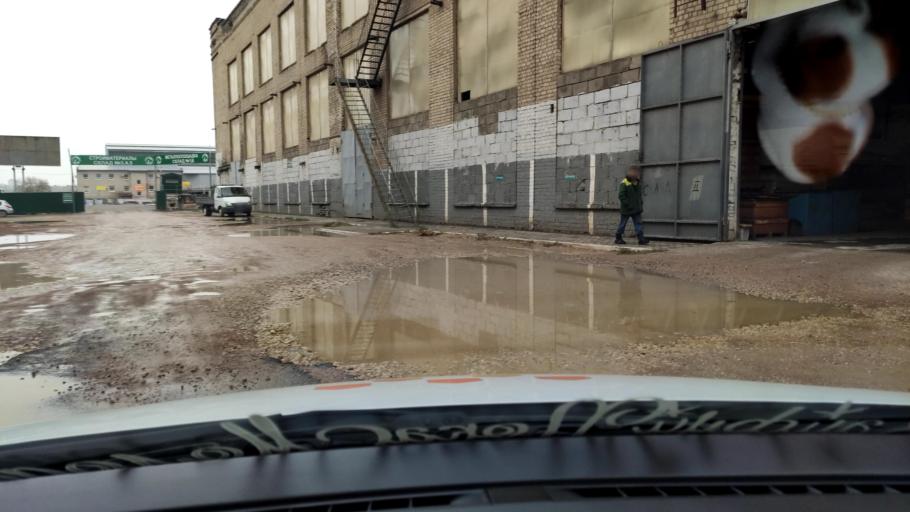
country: RU
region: Voronezj
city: Voronezh
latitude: 51.6881
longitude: 39.1689
